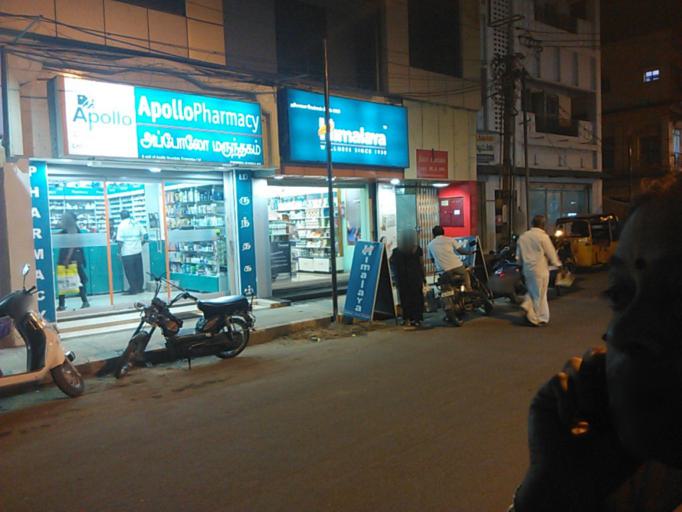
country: IN
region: Tamil Nadu
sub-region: Tiruchchirappalli
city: Tiruchirappalli
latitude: 10.8264
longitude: 78.6987
